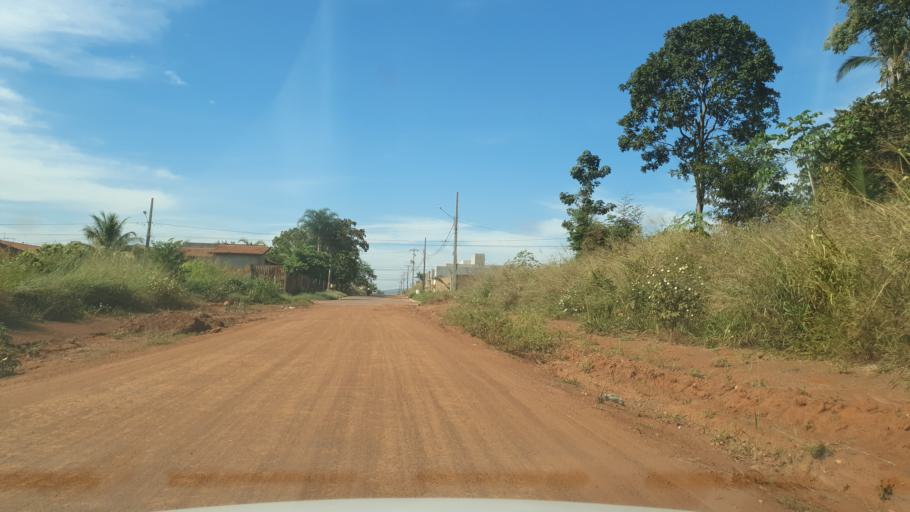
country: BR
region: Mato Grosso
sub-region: Pontes E Lacerda
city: Pontes e Lacerda
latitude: -15.2468
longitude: -59.3167
